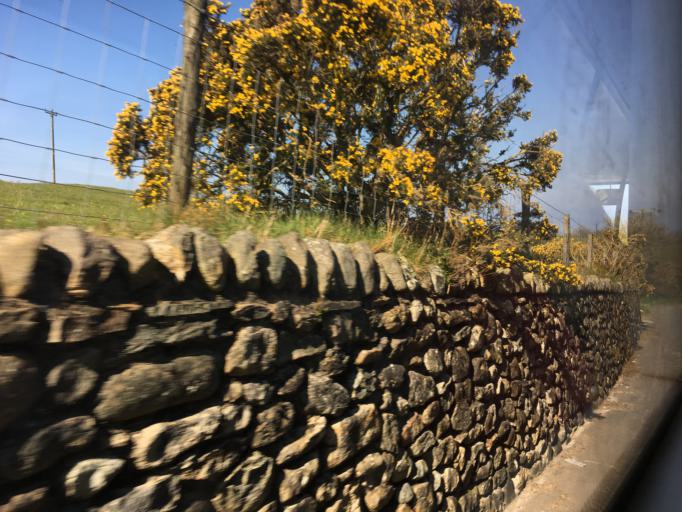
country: GB
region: Wales
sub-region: Gwynedd
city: Llanwnda
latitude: 53.0364
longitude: -4.2847
